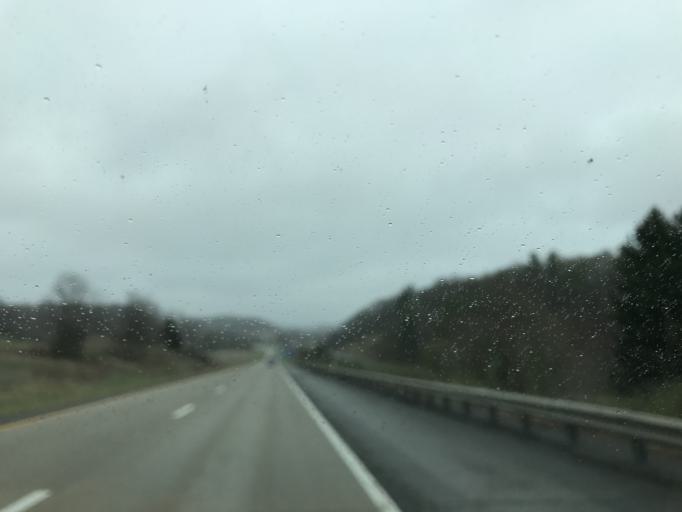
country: US
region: West Virginia
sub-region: Greenbrier County
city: Rainelle
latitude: 37.8411
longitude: -80.7438
